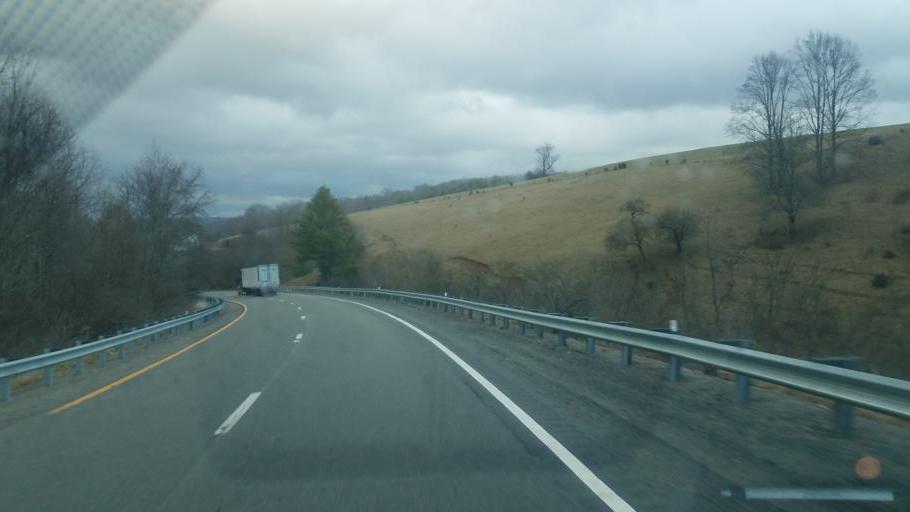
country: US
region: Virginia
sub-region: Giles County
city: Pearisburg
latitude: 37.2749
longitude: -80.7423
